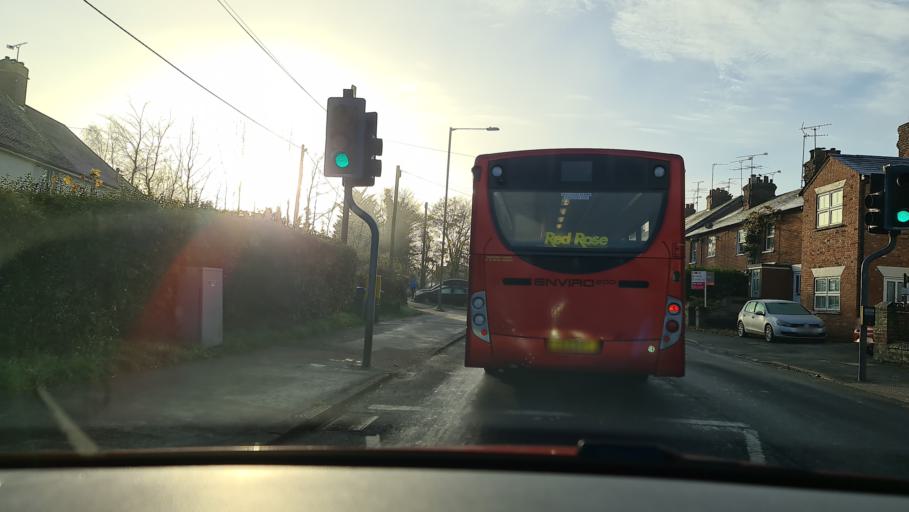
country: GB
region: England
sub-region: Buckinghamshire
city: Wendover
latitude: 51.7661
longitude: -0.7442
